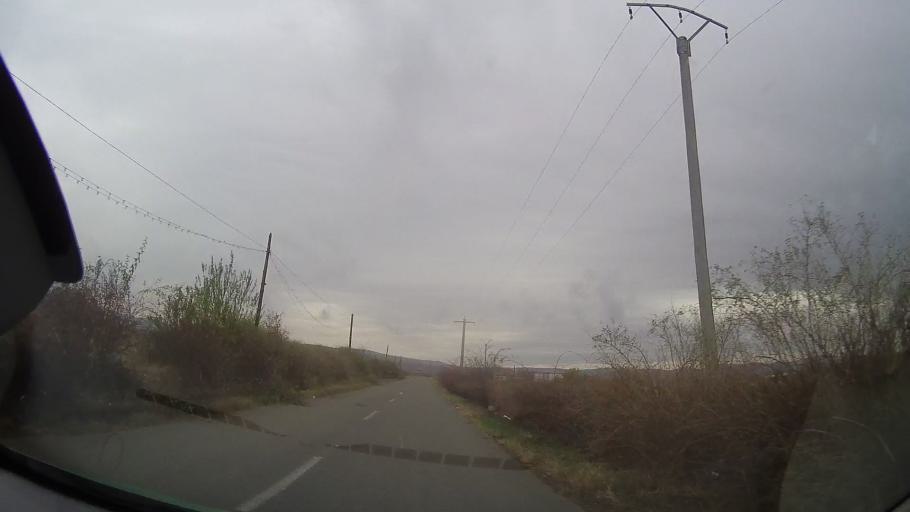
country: RO
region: Prahova
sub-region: Comuna Fantanele
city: Fantanele
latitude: 45.0201
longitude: 26.3804
